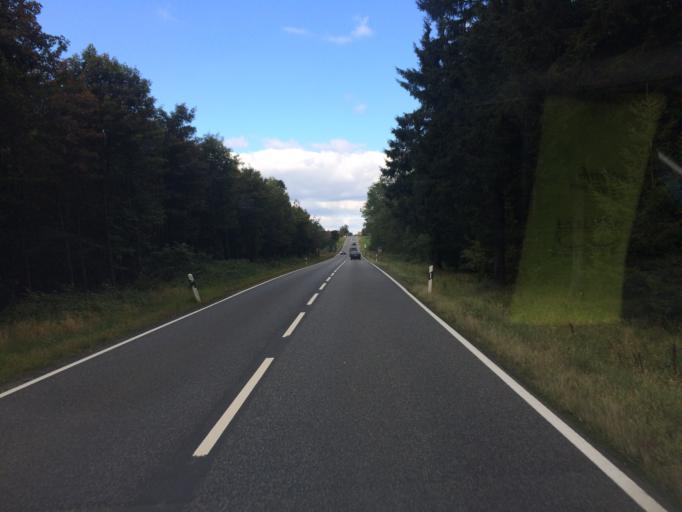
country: DE
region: Rheinland-Pfalz
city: Stein-Neukirch
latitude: 50.6974
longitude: 8.0649
